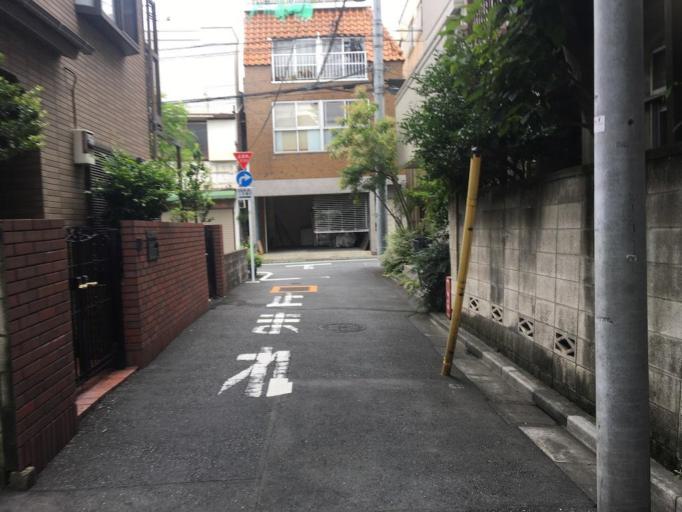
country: JP
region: Tokyo
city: Tokyo
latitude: 35.7348
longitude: 139.7529
